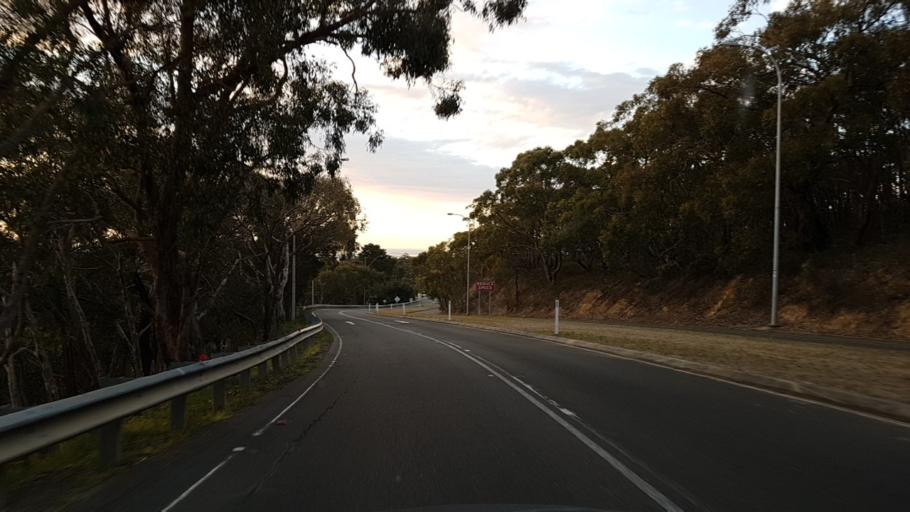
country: AU
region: South Australia
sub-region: Adelaide Hills
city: Crafers
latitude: -34.9821
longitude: 138.6879
